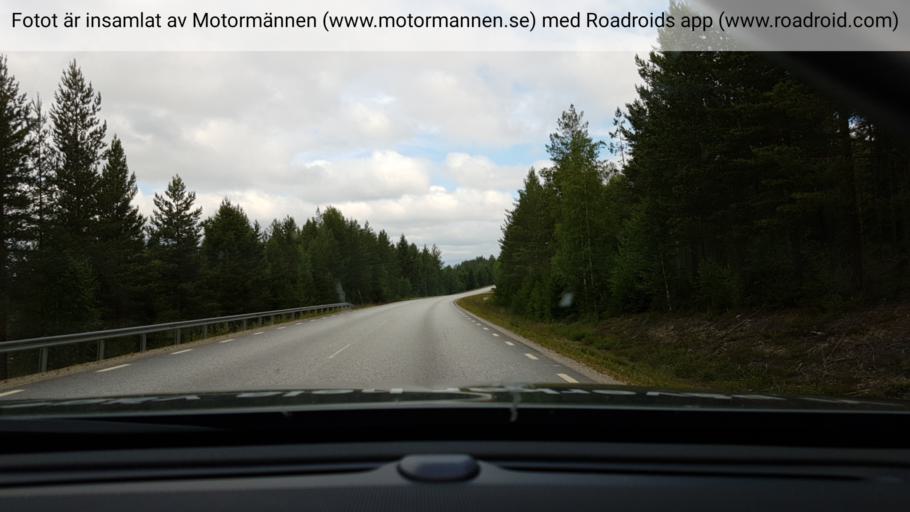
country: SE
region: Vaesterbotten
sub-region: Vindelns Kommun
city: Vindeln
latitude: 64.3536
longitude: 19.4600
